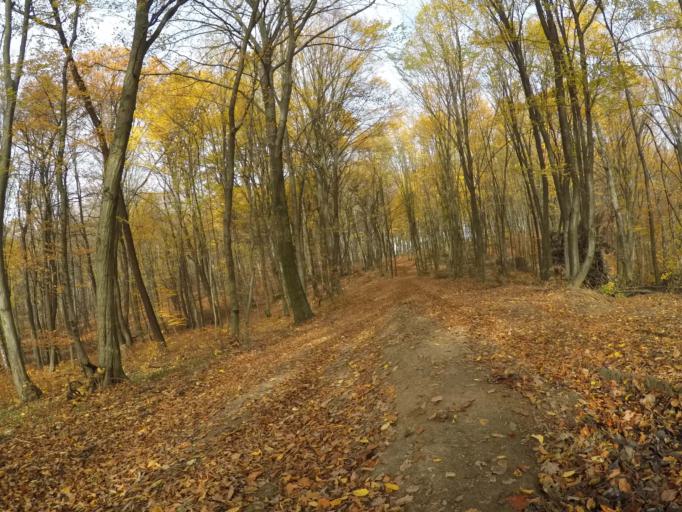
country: SK
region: Presovsky
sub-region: Okres Presov
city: Presov
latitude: 48.9342
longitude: 21.2203
